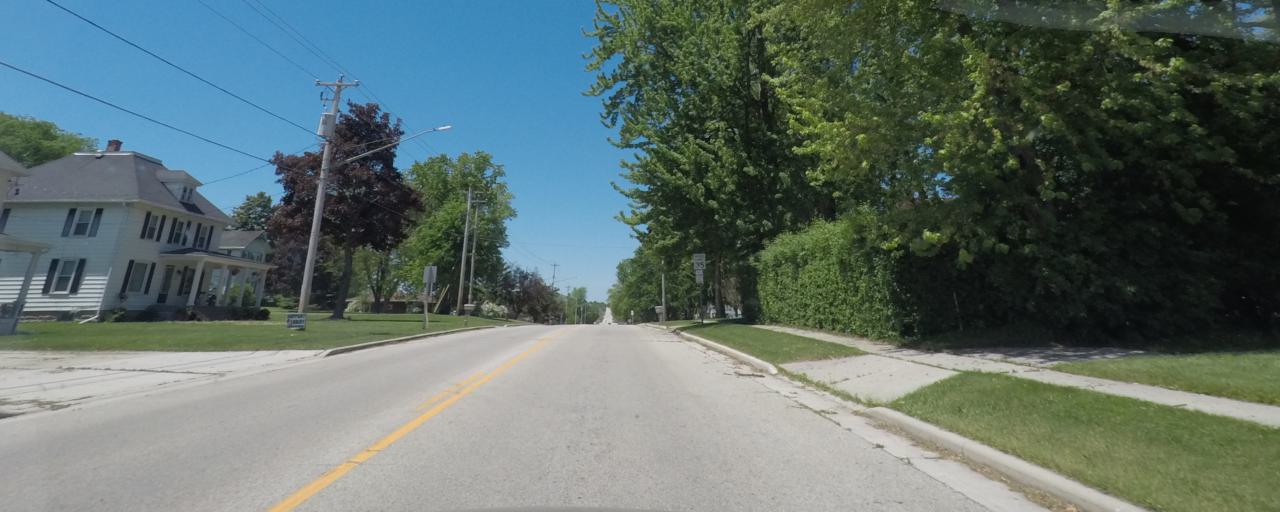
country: US
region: Wisconsin
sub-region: Sheboygan County
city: Plymouth
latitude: 43.6746
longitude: -87.9465
